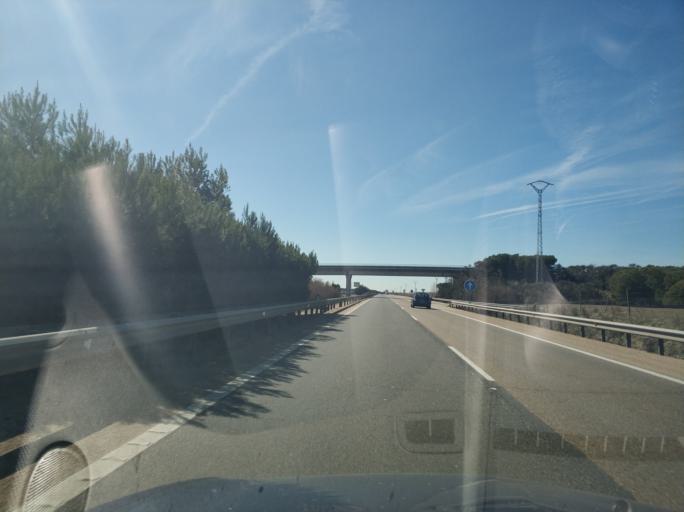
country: ES
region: Castille and Leon
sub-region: Provincia de Valladolid
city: San Miguel del Pino
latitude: 41.5277
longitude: -4.9159
